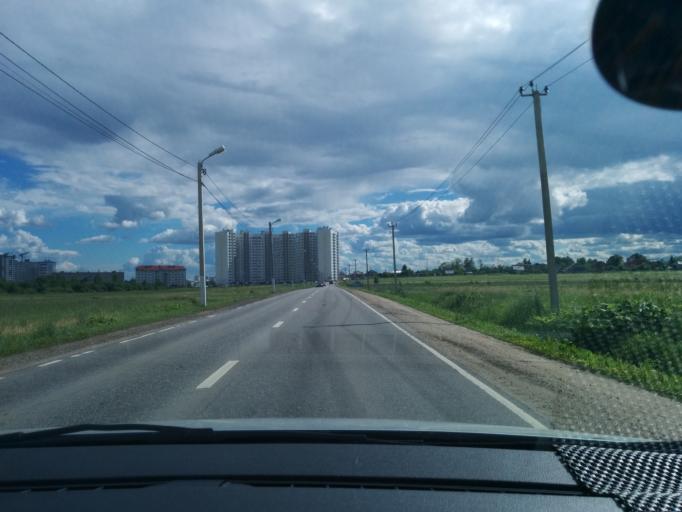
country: RU
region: Moskovskaya
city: Lugovaya
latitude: 56.0339
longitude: 37.4679
